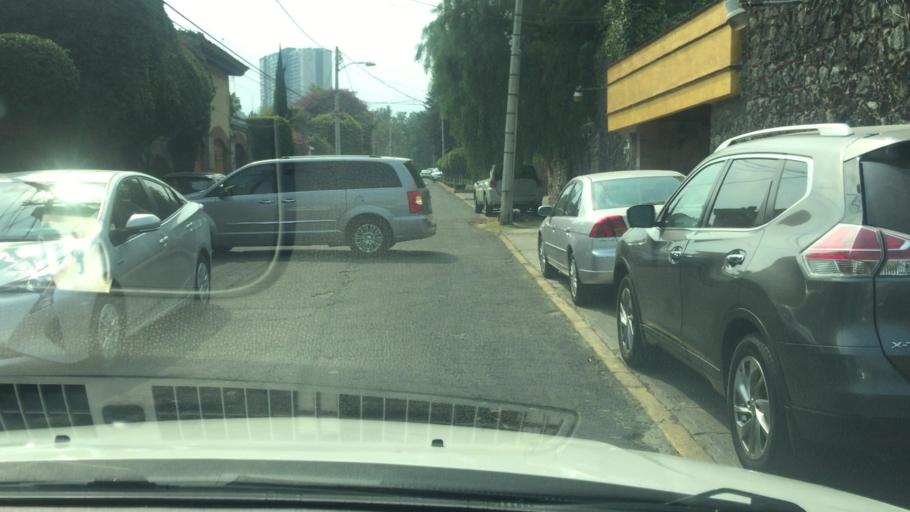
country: MX
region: Mexico City
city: Magdalena Contreras
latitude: 19.3140
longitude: -99.2098
